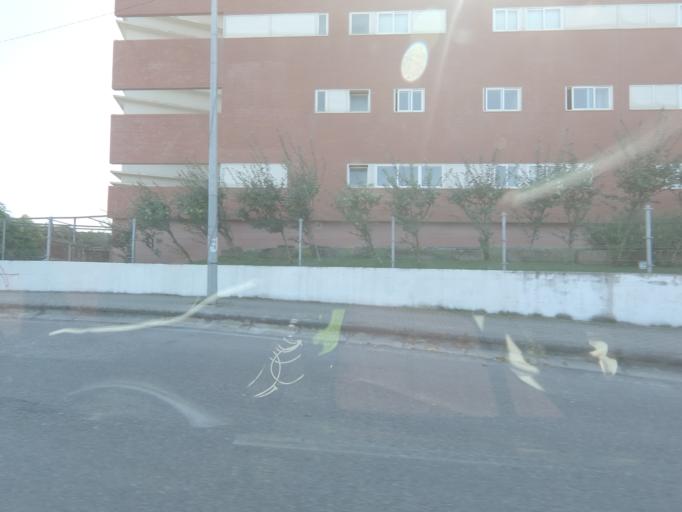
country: PT
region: Setubal
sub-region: Setubal
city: Setubal
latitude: 38.5313
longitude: -8.8973
